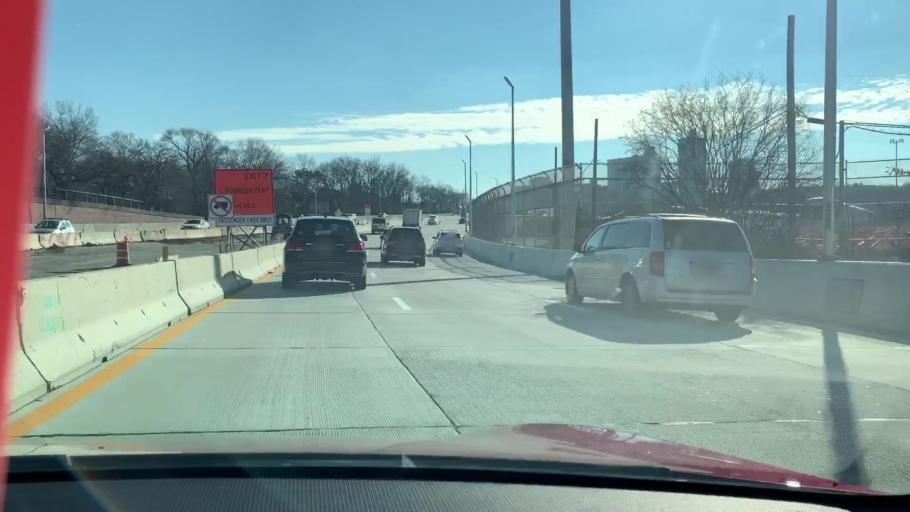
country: US
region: New York
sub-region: Queens County
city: Jamaica
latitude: 40.7213
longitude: -73.8268
